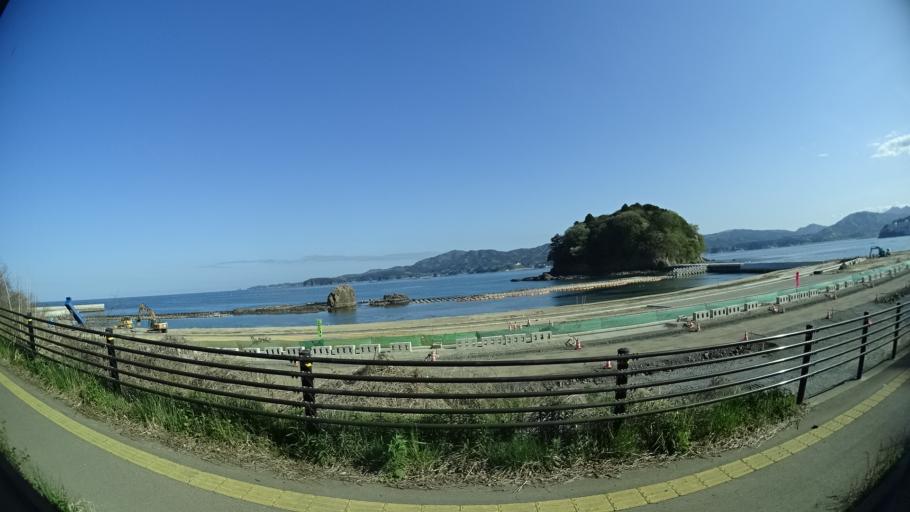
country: JP
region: Miyagi
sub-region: Oshika Gun
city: Onagawa Cho
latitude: 38.6715
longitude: 141.4621
